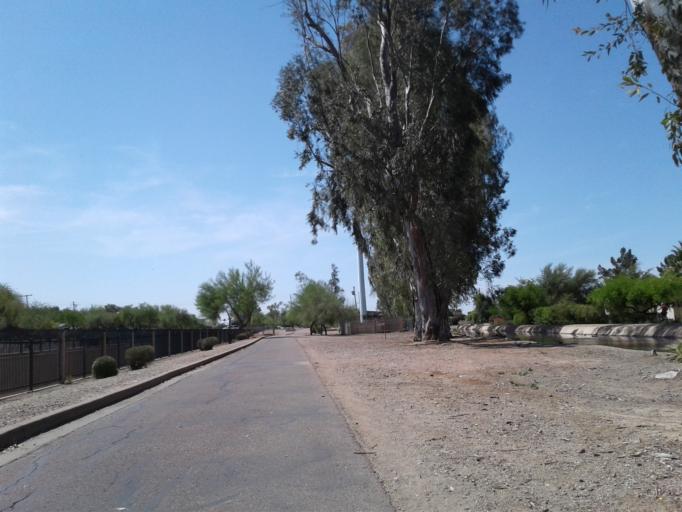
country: US
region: Arizona
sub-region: Maricopa County
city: Phoenix
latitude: 33.5547
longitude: -112.0617
